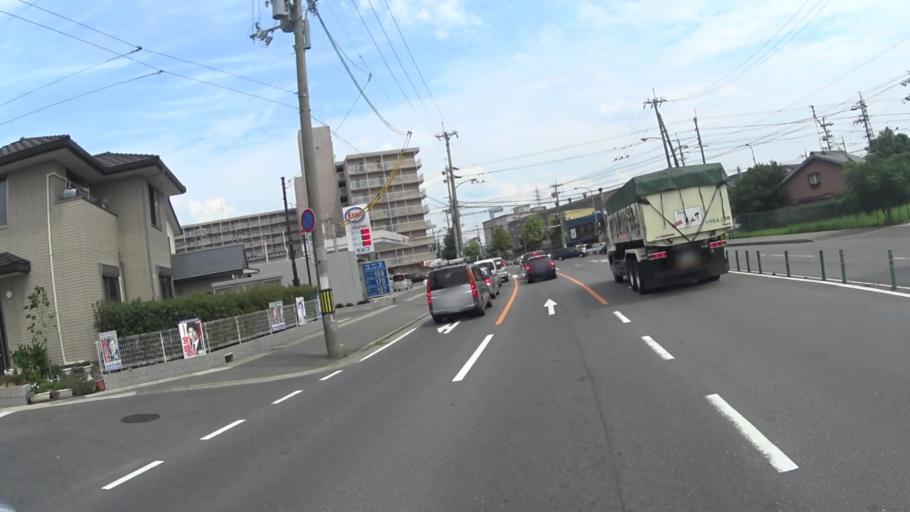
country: JP
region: Kyoto
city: Muko
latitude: 34.9273
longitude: 135.7383
